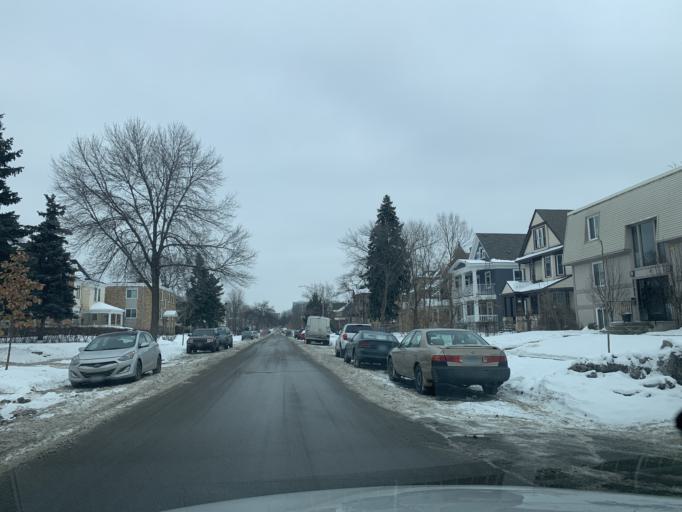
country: US
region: Minnesota
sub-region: Hennepin County
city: Minneapolis
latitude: 44.9530
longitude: -93.2815
